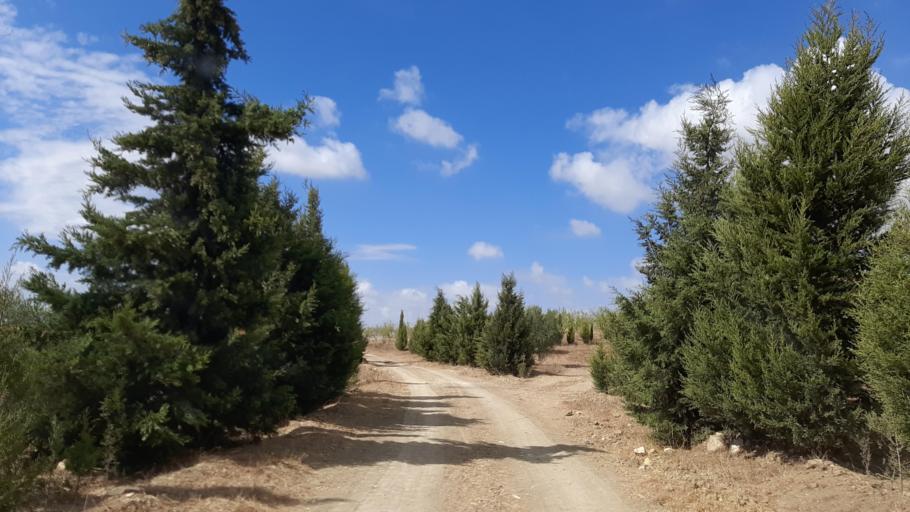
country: TN
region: Zaghwan
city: Zaghouan
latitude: 36.5025
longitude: 10.1823
